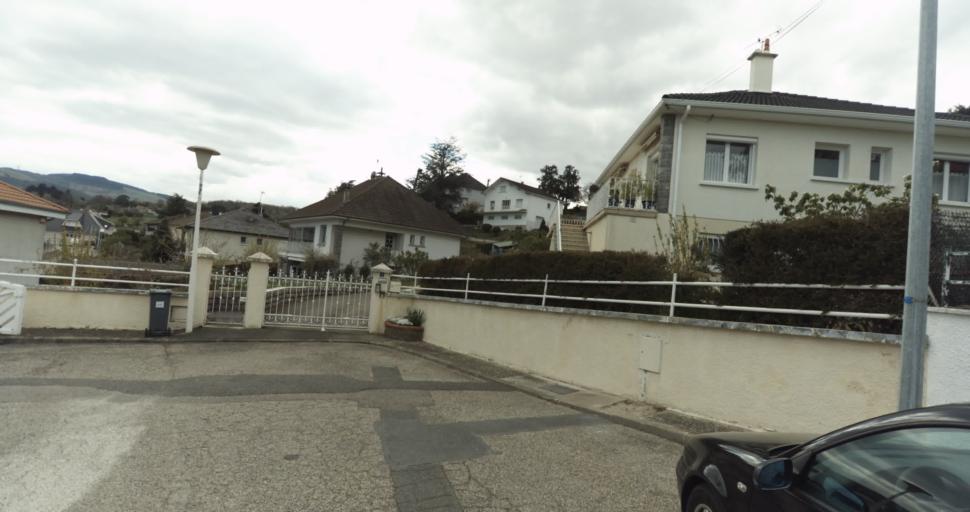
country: FR
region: Rhone-Alpes
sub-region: Departement de la Loire
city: Saint-Jean-Bonnefonds
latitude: 45.4500
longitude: 4.4494
